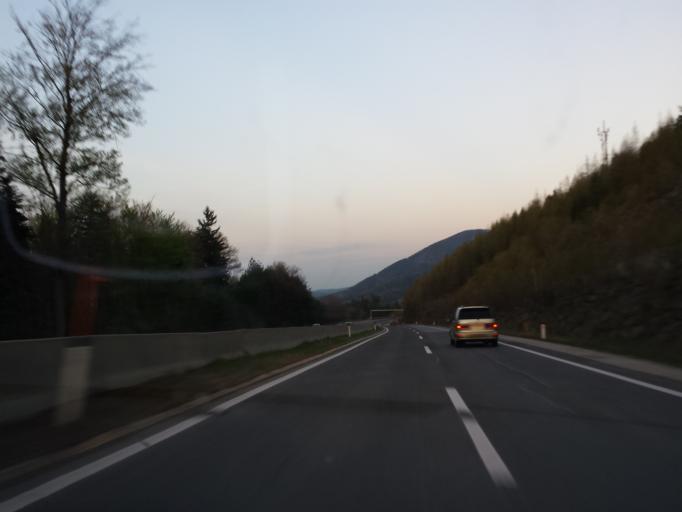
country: AT
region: Lower Austria
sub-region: Politischer Bezirk Neunkirchen
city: Schottwien
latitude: 47.6549
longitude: 15.8950
